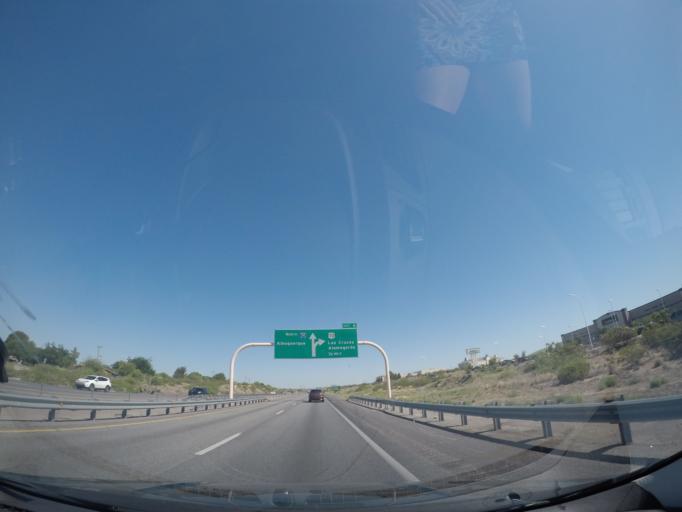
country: US
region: New Mexico
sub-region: Dona Ana County
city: Las Cruces
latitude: 32.3389
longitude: -106.7632
